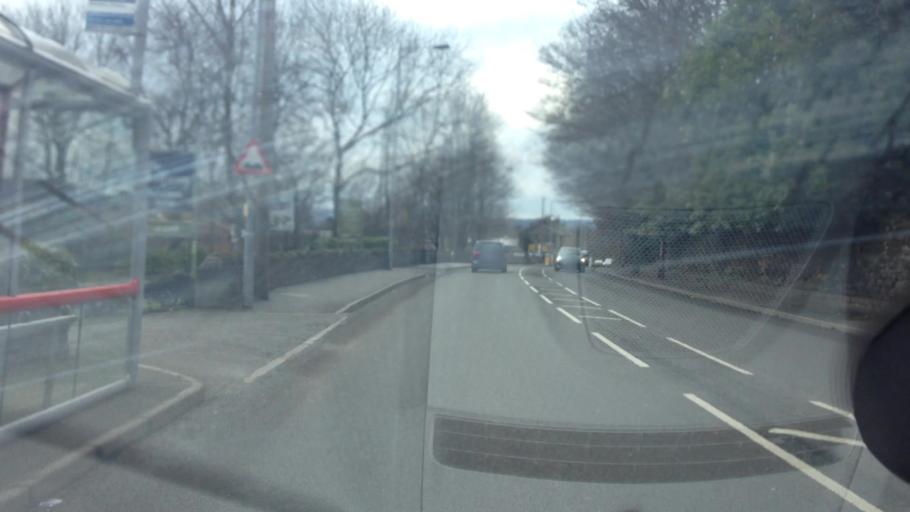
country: GB
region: England
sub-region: Bradford
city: Shipley
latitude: 53.8463
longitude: -1.7522
